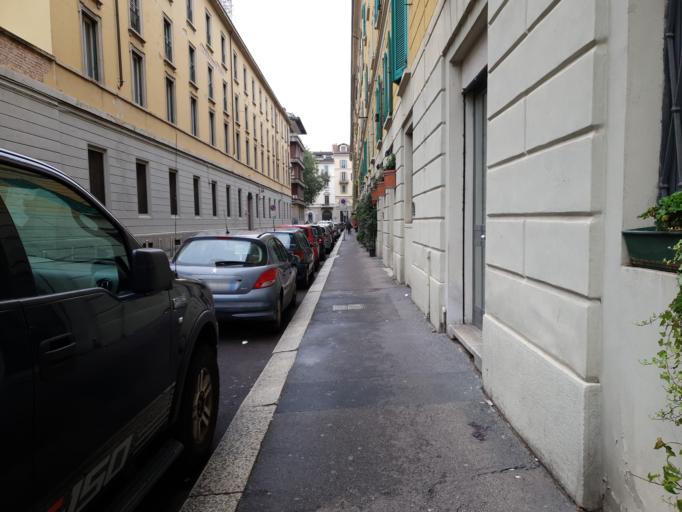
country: IT
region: Lombardy
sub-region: Citta metropolitana di Milano
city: Milano
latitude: 45.4764
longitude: 9.1897
